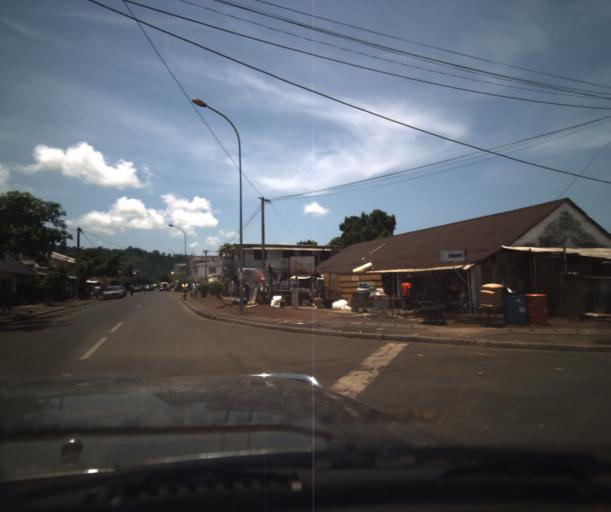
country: CM
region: South-West Province
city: Limbe
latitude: 4.0086
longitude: 9.2075
